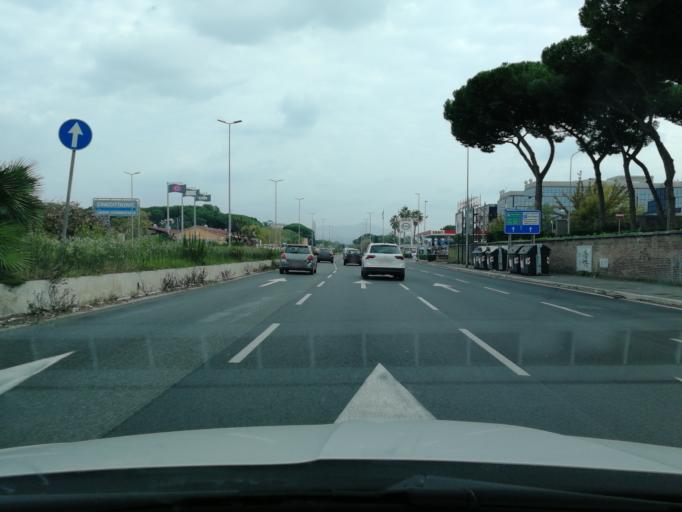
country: IT
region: Latium
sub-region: Citta metropolitana di Roma Capitale
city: Ciampino
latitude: 41.8517
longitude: 12.5708
